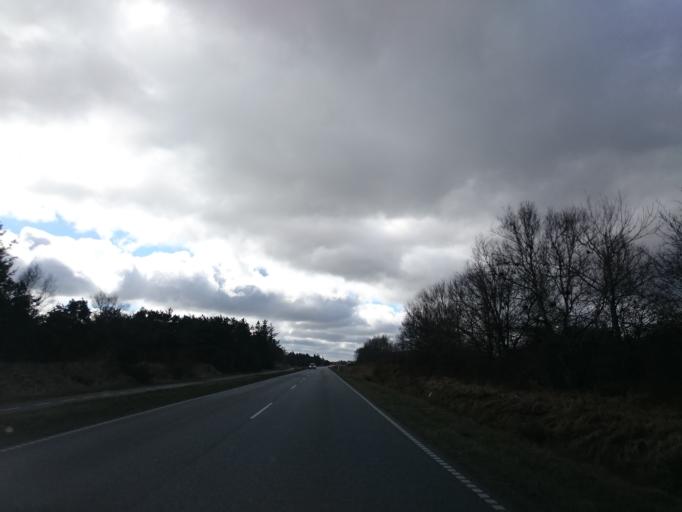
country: DK
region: North Denmark
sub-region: Frederikshavn Kommune
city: Strandby
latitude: 57.6163
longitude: 10.4349
